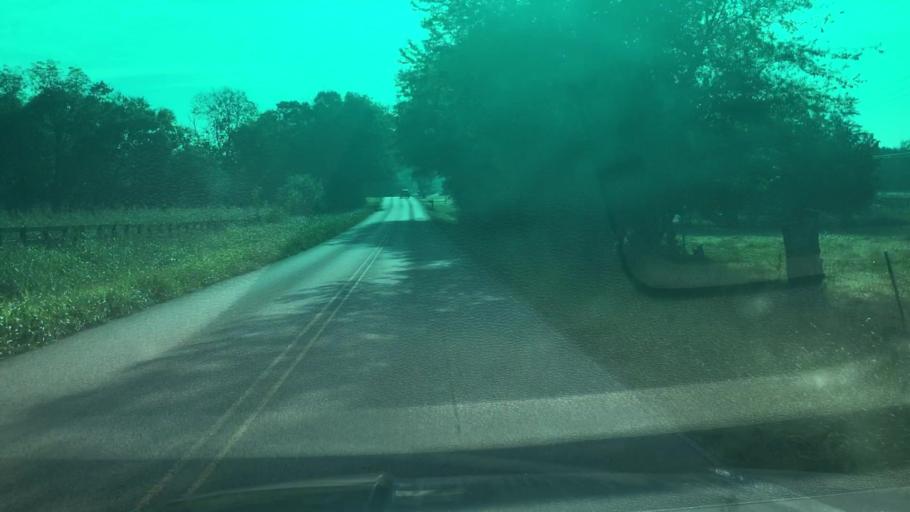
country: US
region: Tennessee
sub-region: Williamson County
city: Thompson's Station
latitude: 35.7894
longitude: -86.8587
